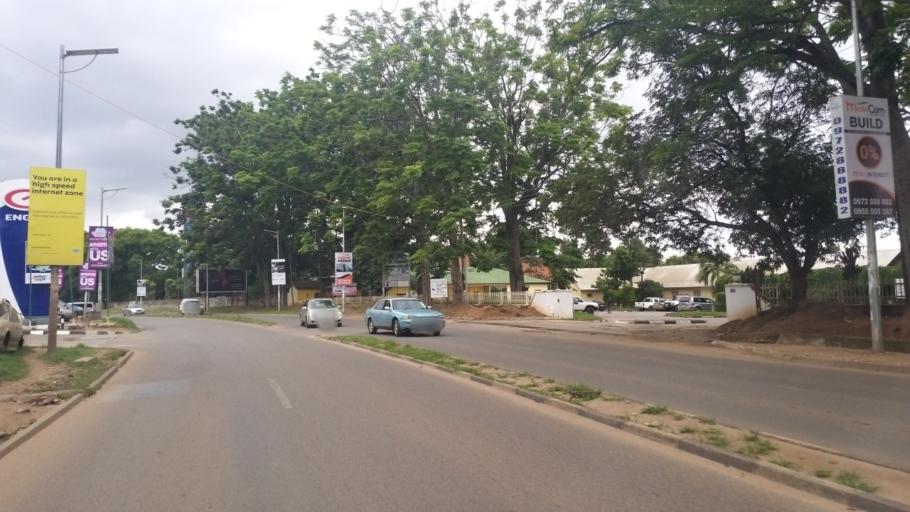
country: ZM
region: Lusaka
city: Lusaka
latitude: -15.4166
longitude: 28.3140
